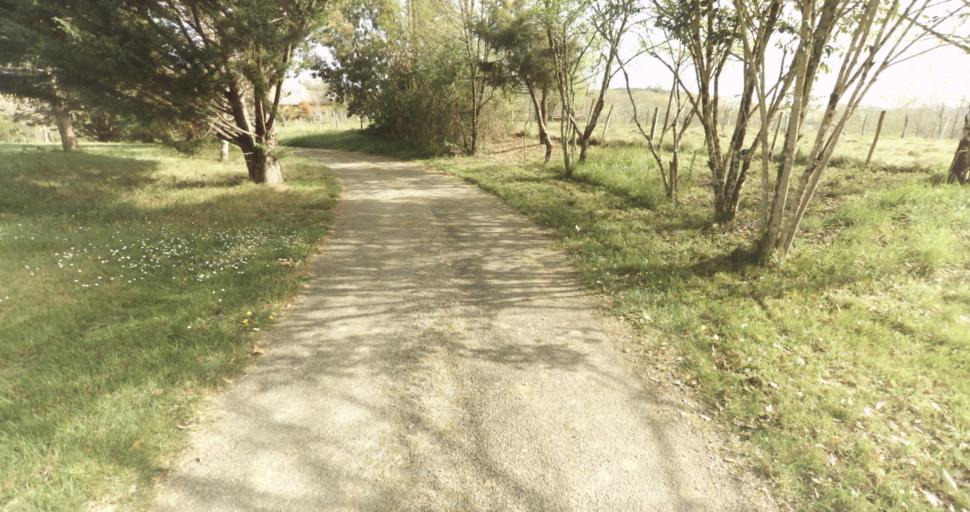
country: FR
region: Midi-Pyrenees
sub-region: Departement du Tarn-et-Garonne
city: Lafrancaise
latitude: 44.1518
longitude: 1.1836
